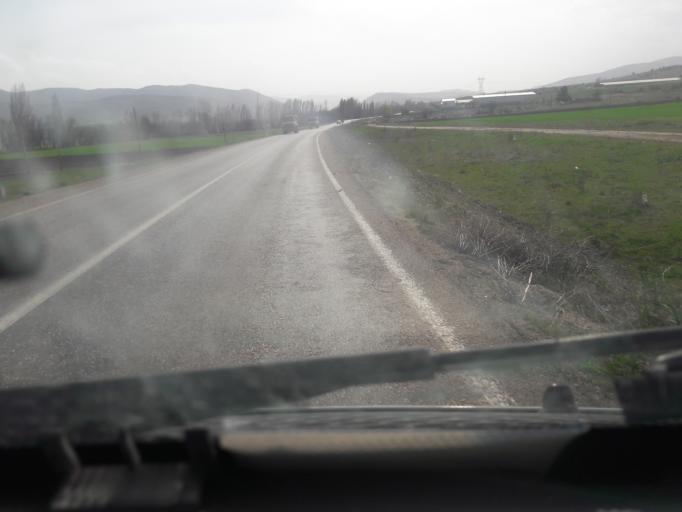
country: TR
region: Gumushane
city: Kelkit
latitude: 40.1324
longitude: 39.3734
